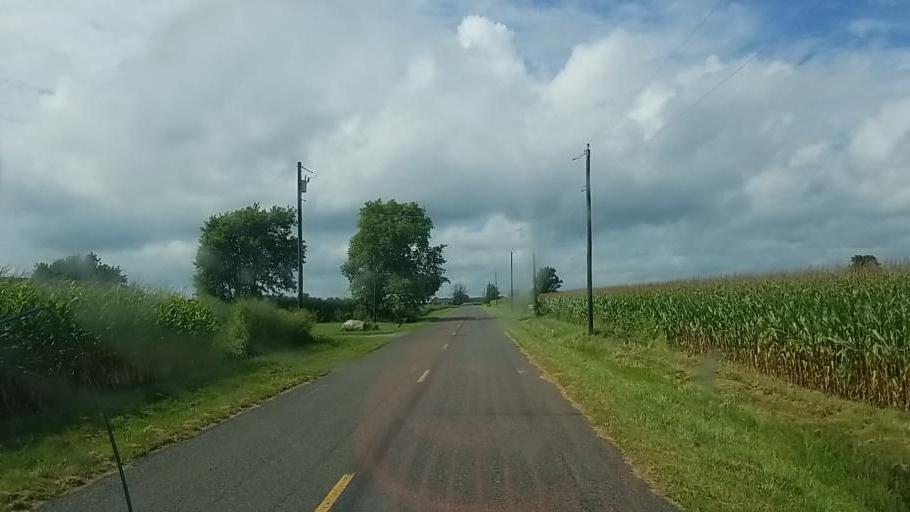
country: US
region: Ohio
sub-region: Hardin County
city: Kenton
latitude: 40.4878
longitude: -83.5159
